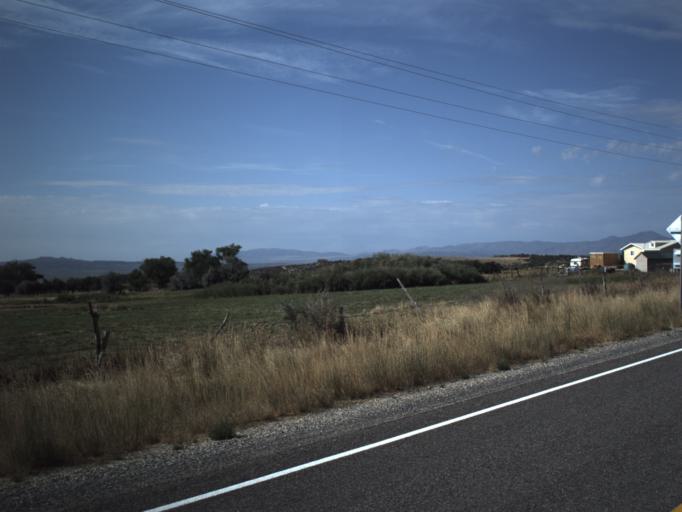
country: US
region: Idaho
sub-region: Cassia County
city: Burley
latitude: 41.8194
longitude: -113.4074
